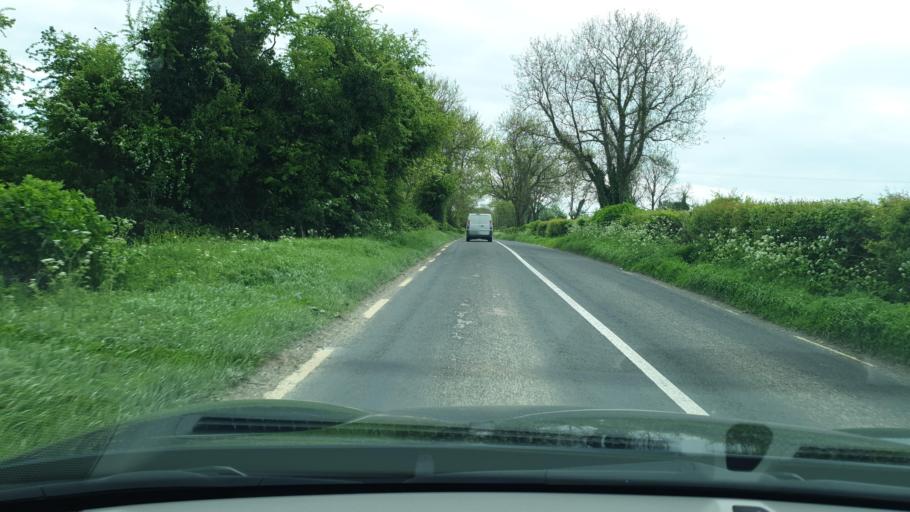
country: IE
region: Leinster
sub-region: An Mhi
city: Navan
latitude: 53.7178
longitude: -6.6972
